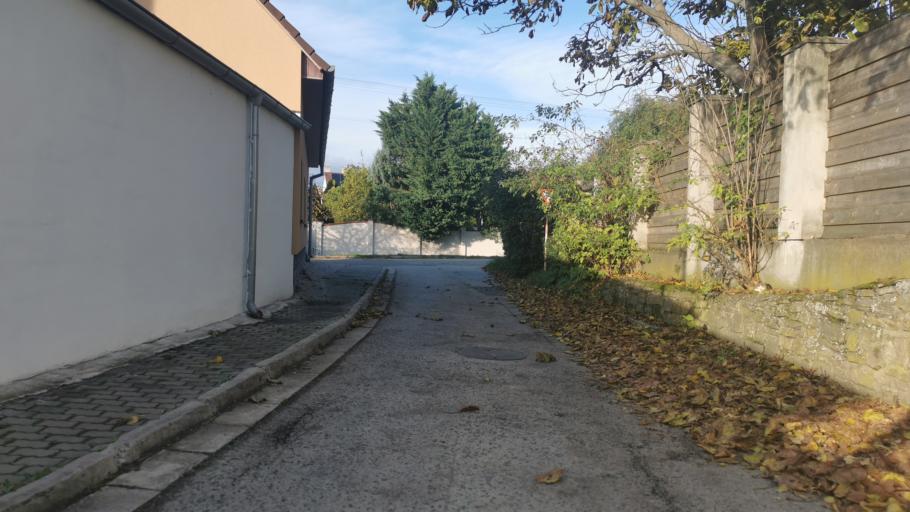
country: SK
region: Trnavsky
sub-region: Okres Skalica
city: Skalica
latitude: 48.8427
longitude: 17.2392
